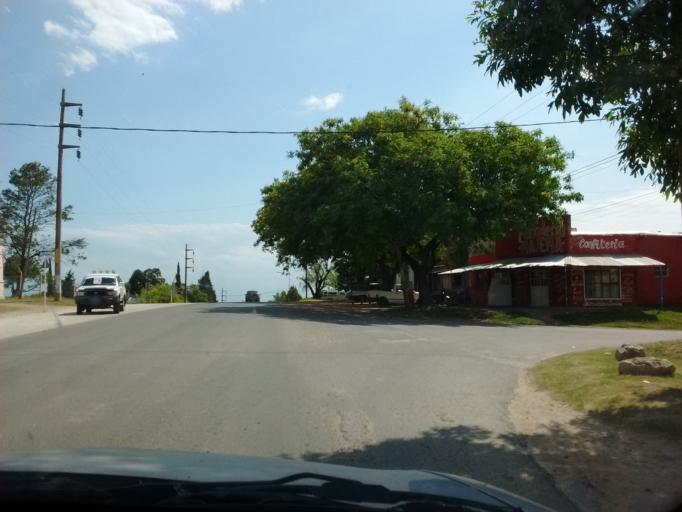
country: AR
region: Entre Rios
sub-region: Departamento de Victoria
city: Victoria
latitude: -32.6275
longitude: -60.1411
